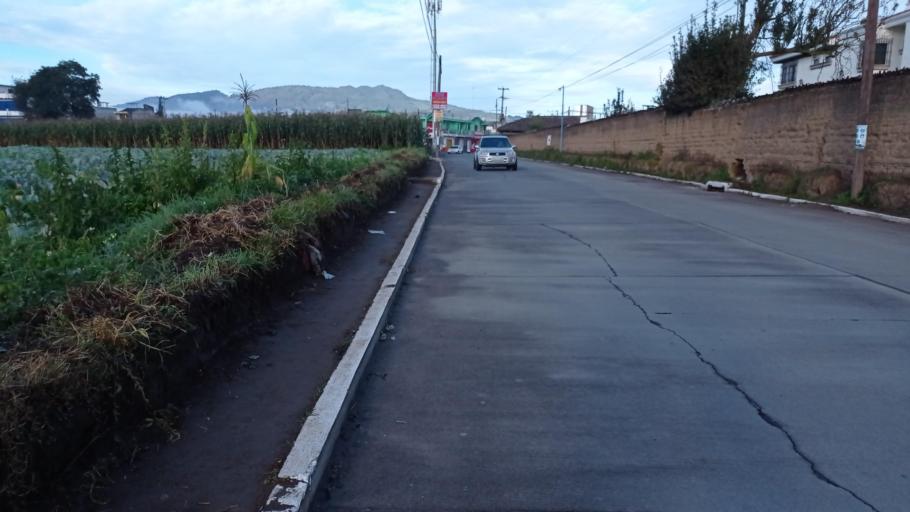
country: GT
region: Quetzaltenango
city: Olintepeque
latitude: 14.8657
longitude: -91.5117
